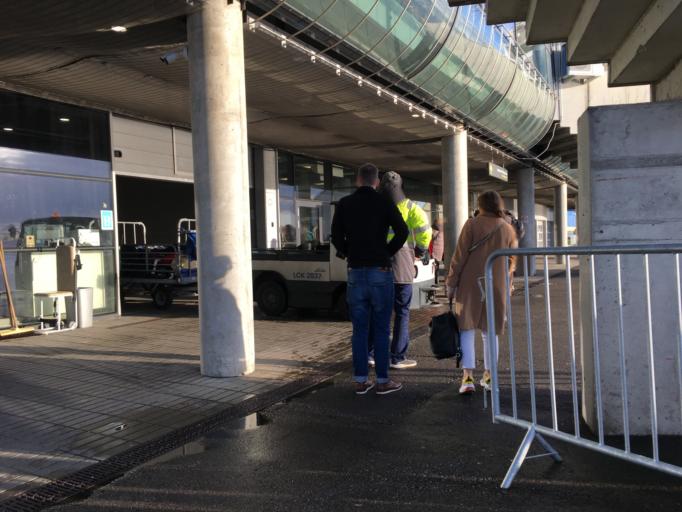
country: LT
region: Kauno apskritis
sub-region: Kauno rajonas
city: Karmelava
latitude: 54.9667
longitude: 24.0734
